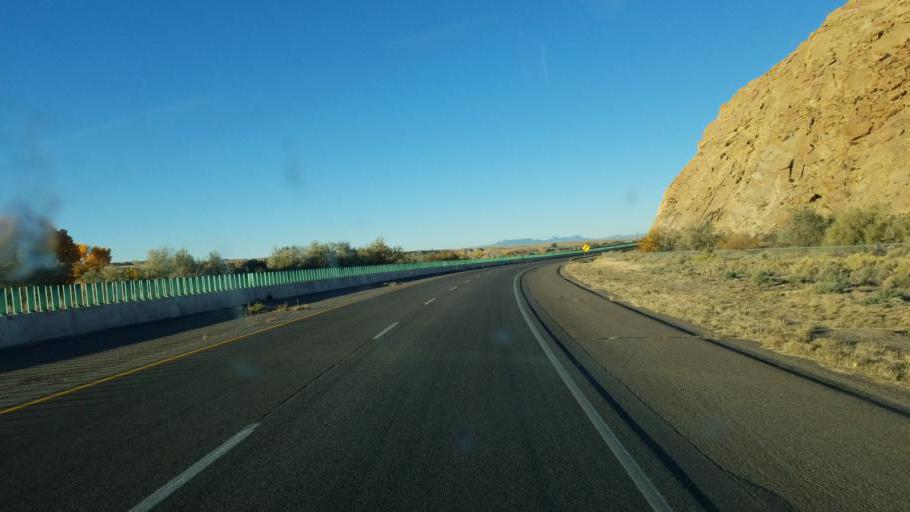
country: US
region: New Mexico
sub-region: San Juan County
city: Waterflow
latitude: 36.7482
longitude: -108.5332
